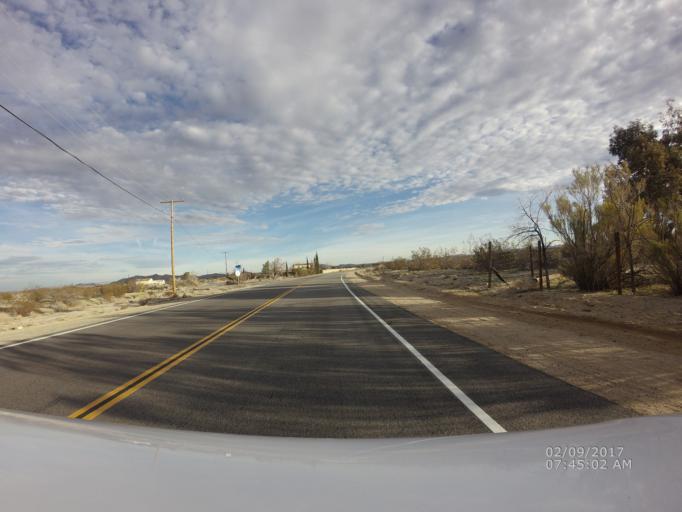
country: US
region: California
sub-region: Los Angeles County
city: Lake Los Angeles
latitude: 34.5442
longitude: -117.8354
